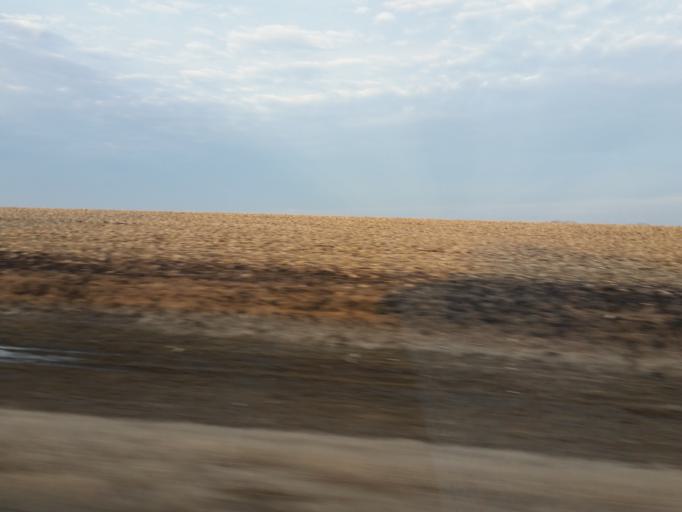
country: US
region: North Dakota
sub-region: Traill County
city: Mayville
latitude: 47.5490
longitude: -97.4531
